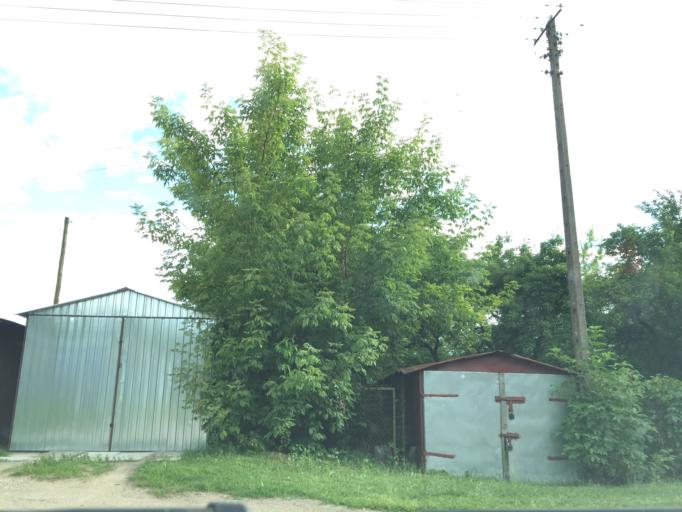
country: PL
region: Podlasie
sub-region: Suwalki
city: Suwalki
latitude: 54.1150
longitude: 22.9310
